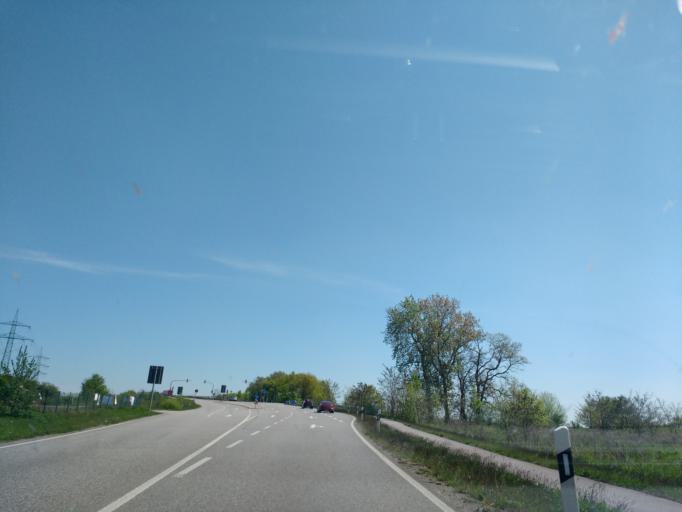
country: DE
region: Saxony-Anhalt
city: Dolbau
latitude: 51.4784
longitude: 12.0733
